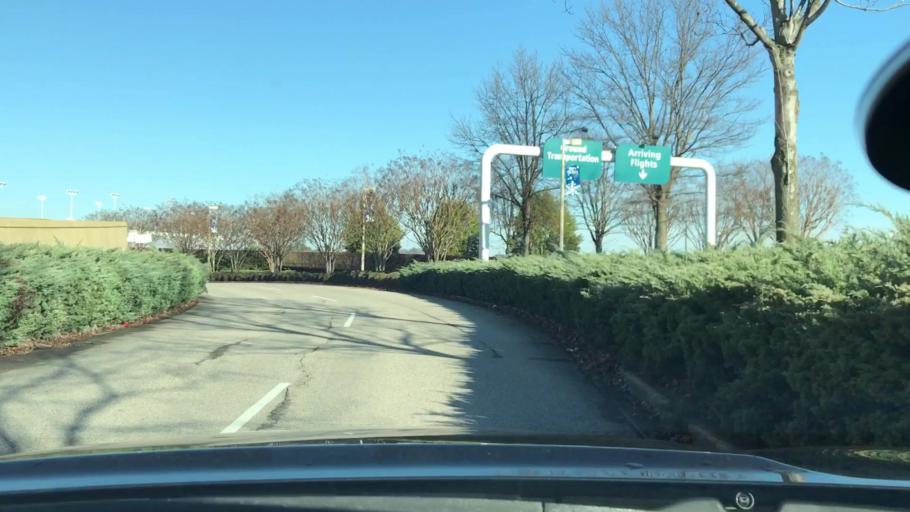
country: US
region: Alabama
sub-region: Jefferson County
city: Tarrant
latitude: 33.5612
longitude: -86.7496
